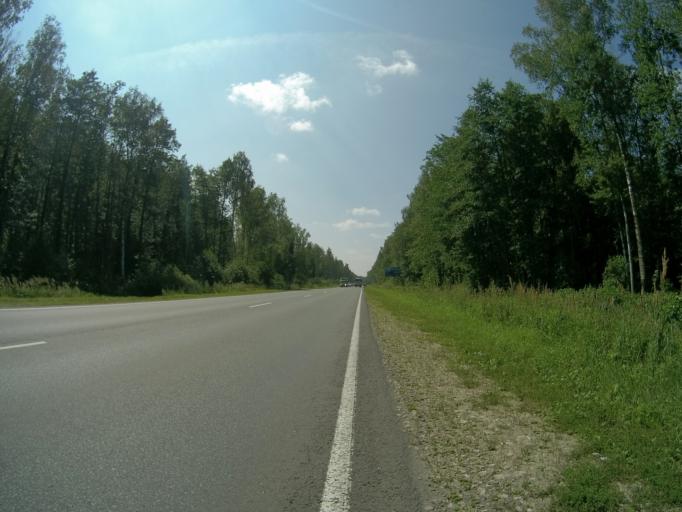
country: RU
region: Vladimir
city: Anopino
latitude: 55.6737
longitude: 40.7379
